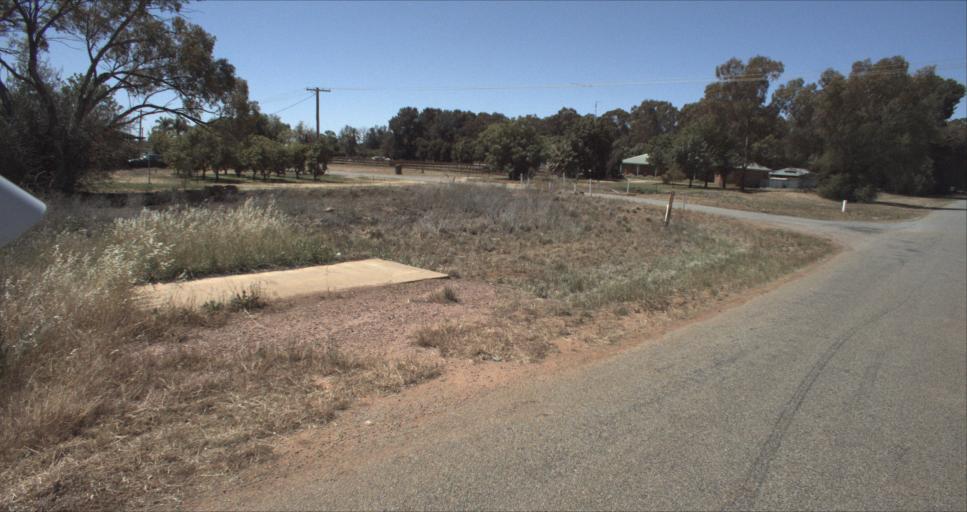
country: AU
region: New South Wales
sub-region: Leeton
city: Leeton
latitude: -34.5310
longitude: 146.3327
